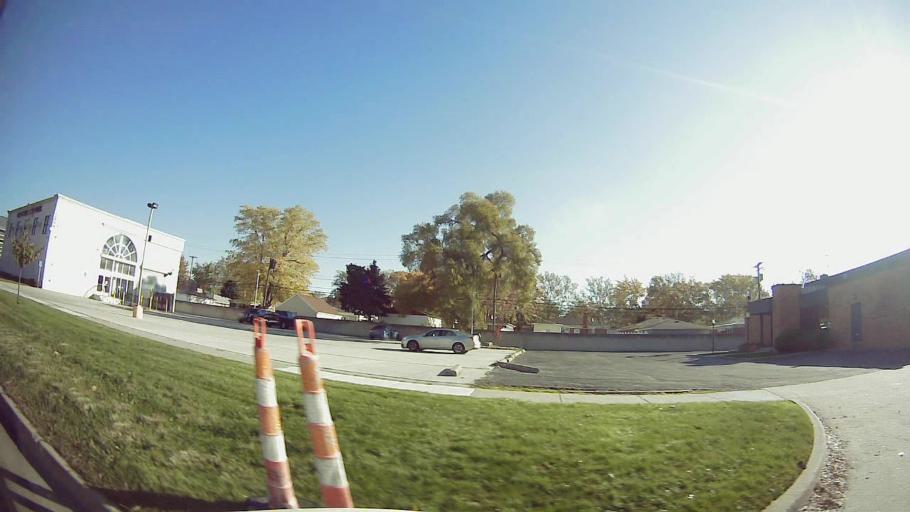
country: US
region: Michigan
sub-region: Oakland County
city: Oak Park
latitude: 42.4563
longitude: -83.2008
